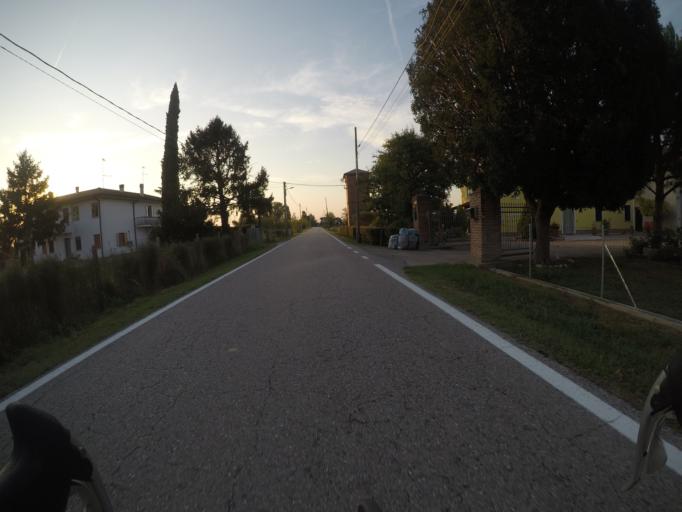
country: IT
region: Veneto
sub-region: Provincia di Rovigo
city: San Bellino
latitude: 45.0066
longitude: 11.5737
